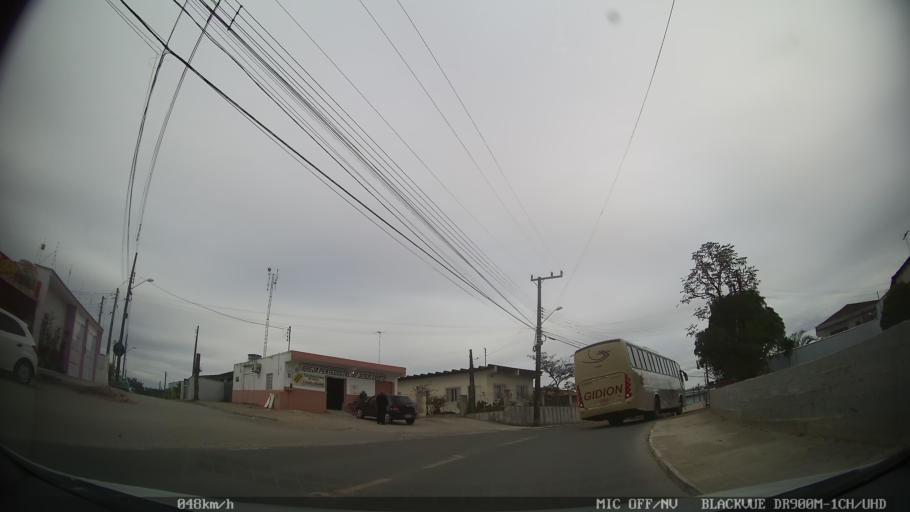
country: BR
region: Santa Catarina
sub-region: Joinville
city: Joinville
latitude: -26.3321
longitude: -48.9062
